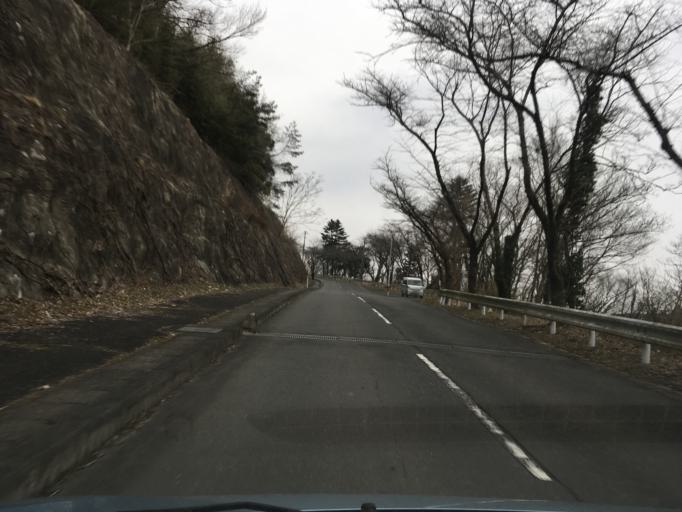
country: JP
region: Miyagi
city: Wakuya
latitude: 38.6610
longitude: 141.2764
